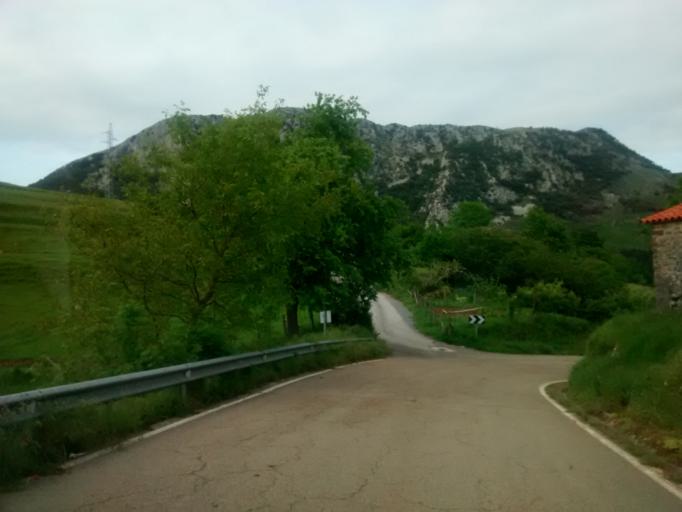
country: ES
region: Cantabria
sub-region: Provincia de Cantabria
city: San Vicente de la Barquera
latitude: 43.2539
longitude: -4.4156
